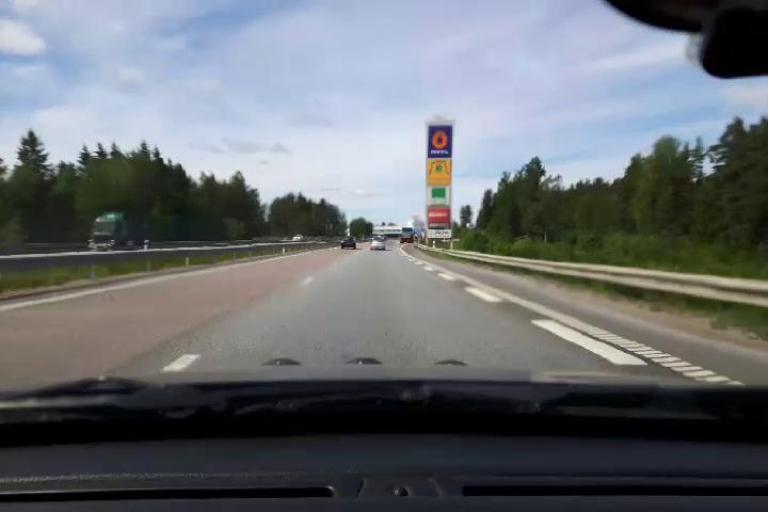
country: SE
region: Gaevleborg
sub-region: Gavle Kommun
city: Gavle
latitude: 60.6460
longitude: 17.1232
